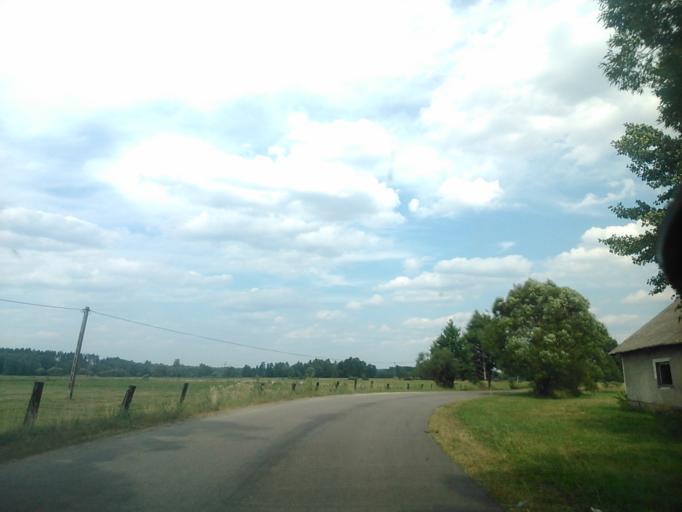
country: PL
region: Masovian Voivodeship
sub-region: Powiat ostrolecki
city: Czarnia
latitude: 53.3602
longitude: 21.1932
